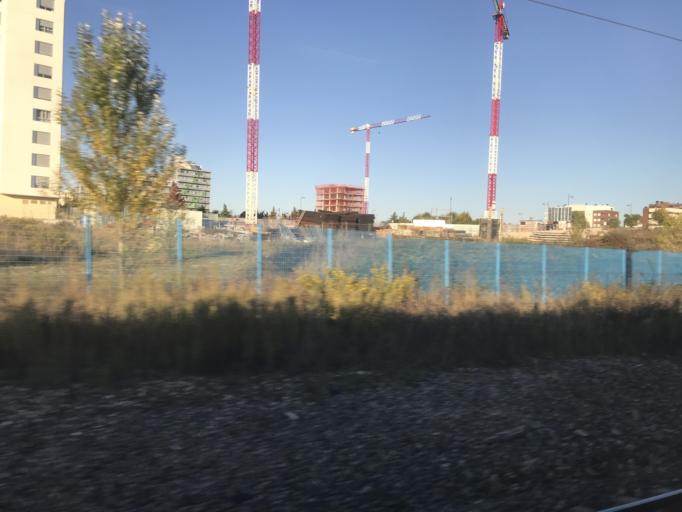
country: ES
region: Basque Country
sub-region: Provincia de Alava
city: Gasteiz / Vitoria
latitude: 42.8478
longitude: -2.6968
